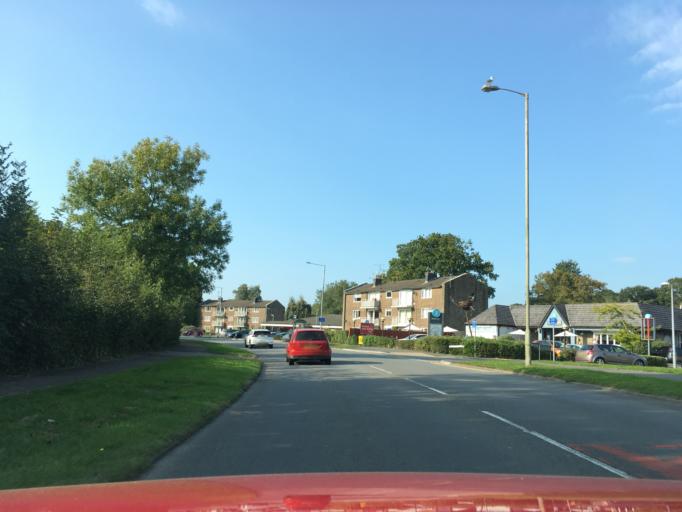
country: GB
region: Wales
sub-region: Torfaen County Borough
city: Cwmbran
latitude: 51.6450
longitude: -3.0069
